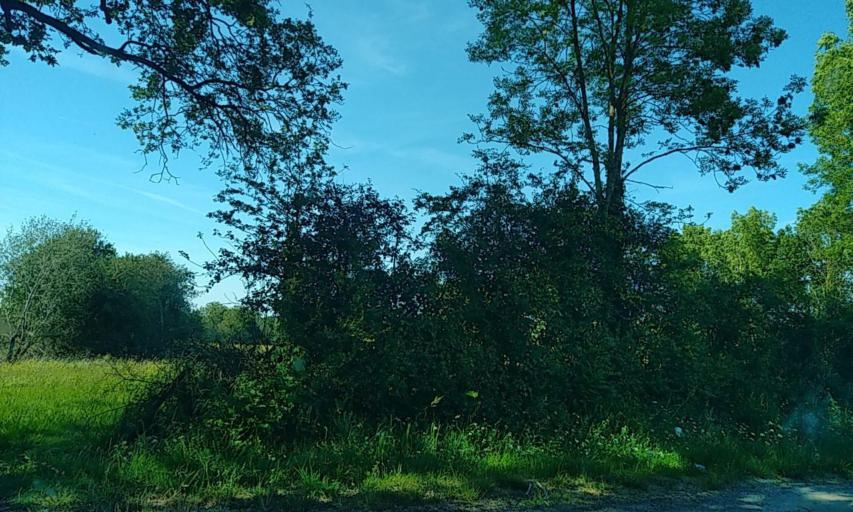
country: FR
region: Poitou-Charentes
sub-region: Departement des Deux-Sevres
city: Boisme
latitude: 46.8068
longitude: -0.4104
